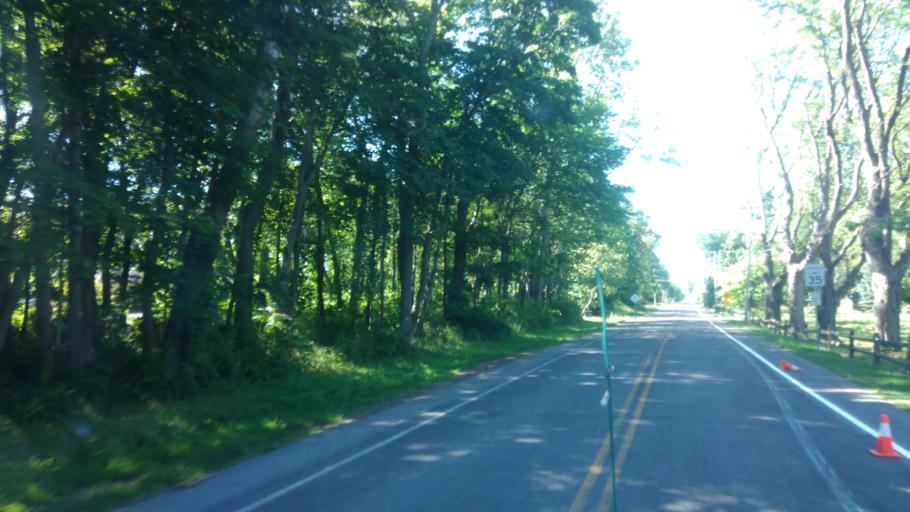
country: US
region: New York
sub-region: Monroe County
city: Webster
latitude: 43.2559
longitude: -77.4686
